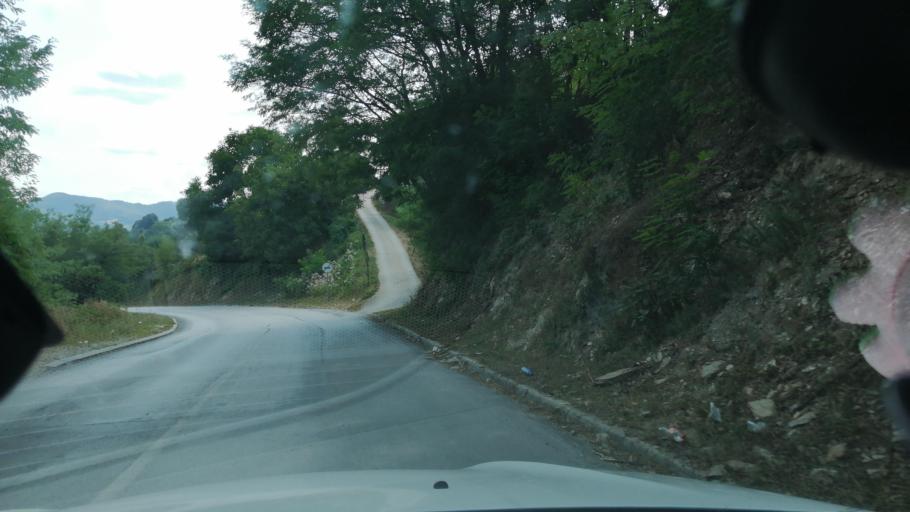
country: RS
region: Central Serbia
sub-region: Moravicki Okrug
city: Ivanjica
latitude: 43.6200
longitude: 20.2378
